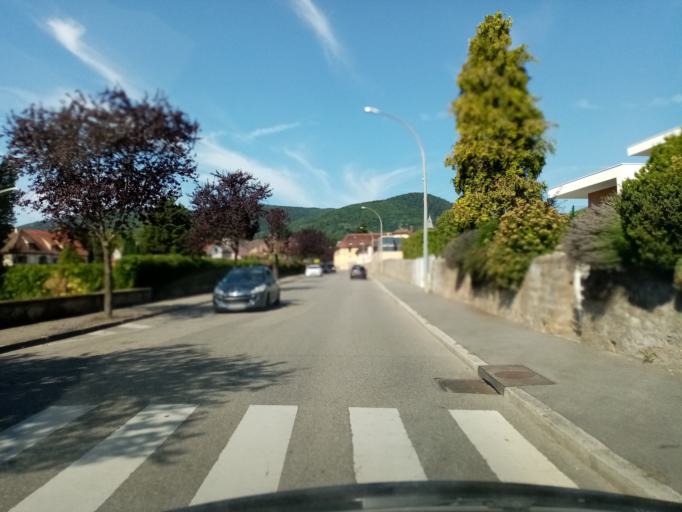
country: FR
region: Alsace
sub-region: Departement du Haut-Rhin
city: Ribeauville
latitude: 48.1946
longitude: 7.3280
